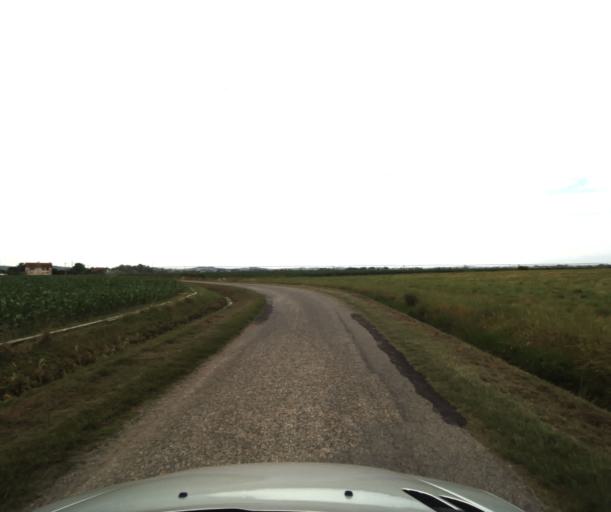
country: FR
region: Midi-Pyrenees
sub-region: Departement de la Haute-Garonne
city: Lacasse
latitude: 43.4216
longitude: 1.2594
